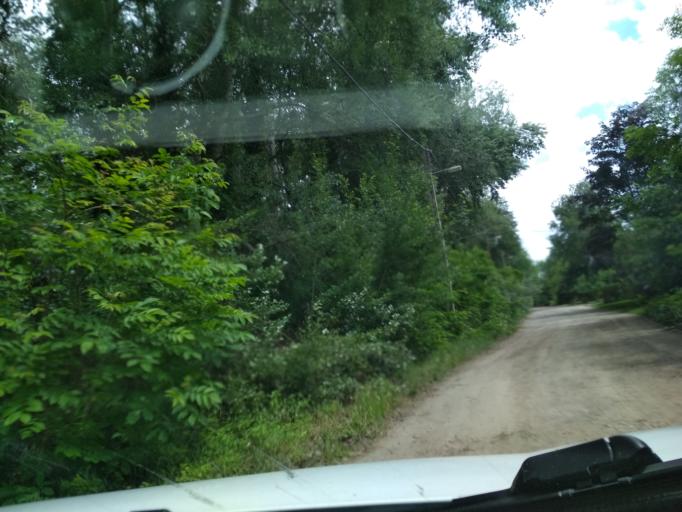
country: HU
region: Jasz-Nagykun-Szolnok
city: Tiszafured
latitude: 47.6195
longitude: 20.7385
